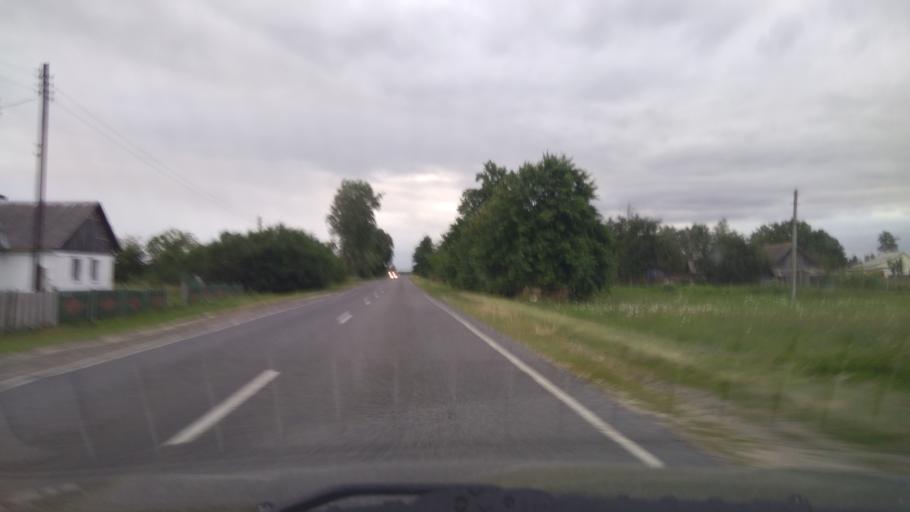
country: BY
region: Brest
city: Byaroza
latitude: 52.4246
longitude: 24.9811
